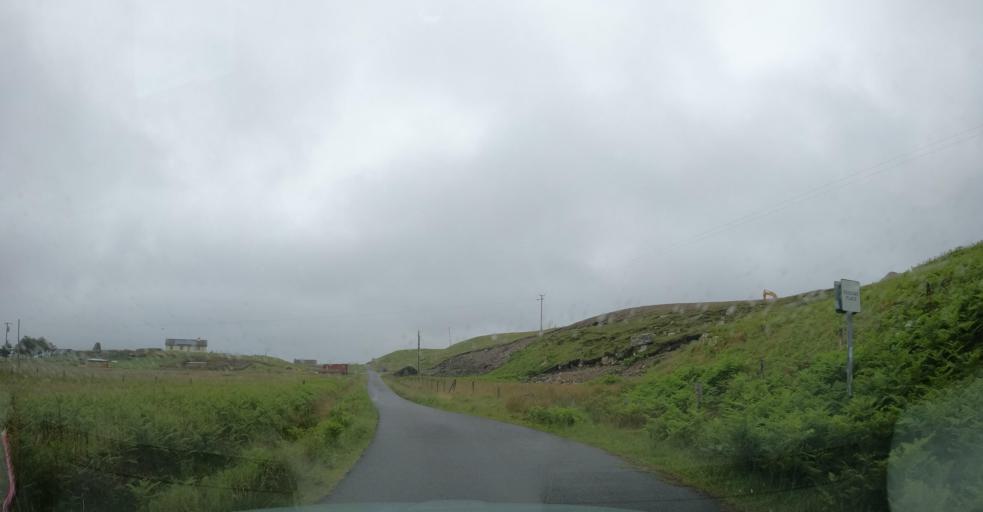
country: GB
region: Scotland
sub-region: Eilean Siar
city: Isle of North Uist
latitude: 57.5516
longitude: -7.2087
